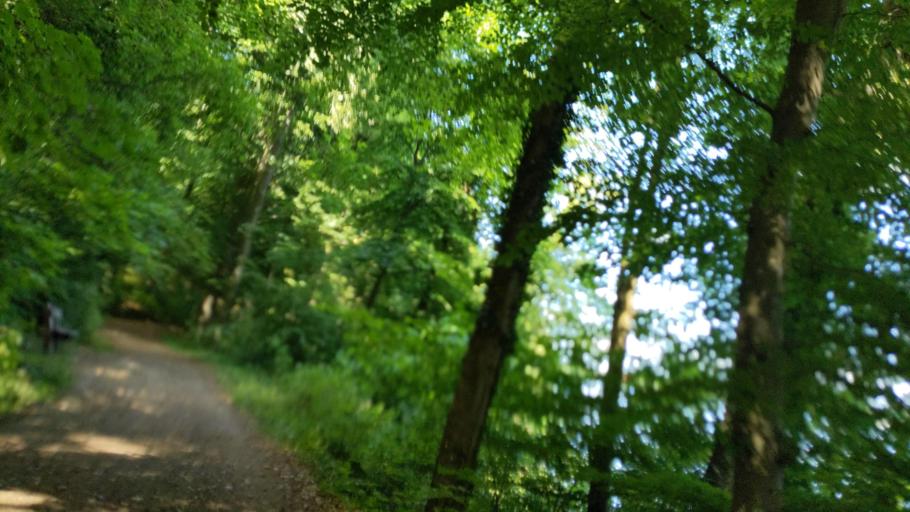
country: DE
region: Schleswig-Holstein
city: Schmilau
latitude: 53.6888
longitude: 10.7539
